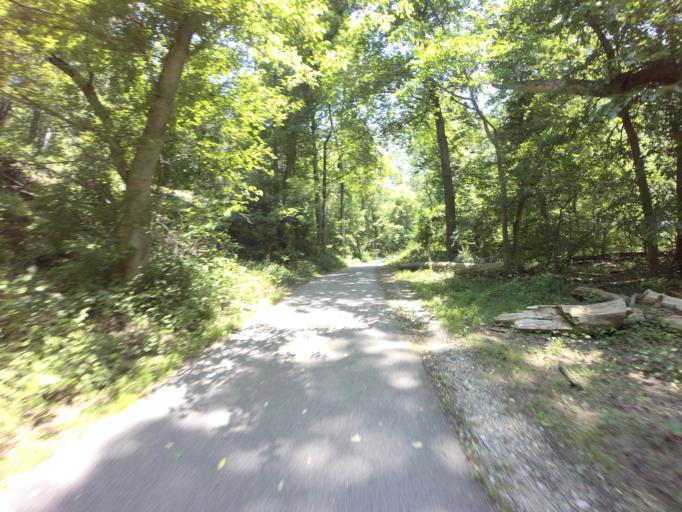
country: US
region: Maryland
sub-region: Howard County
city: West Elkridge
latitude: 39.2313
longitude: -76.7334
